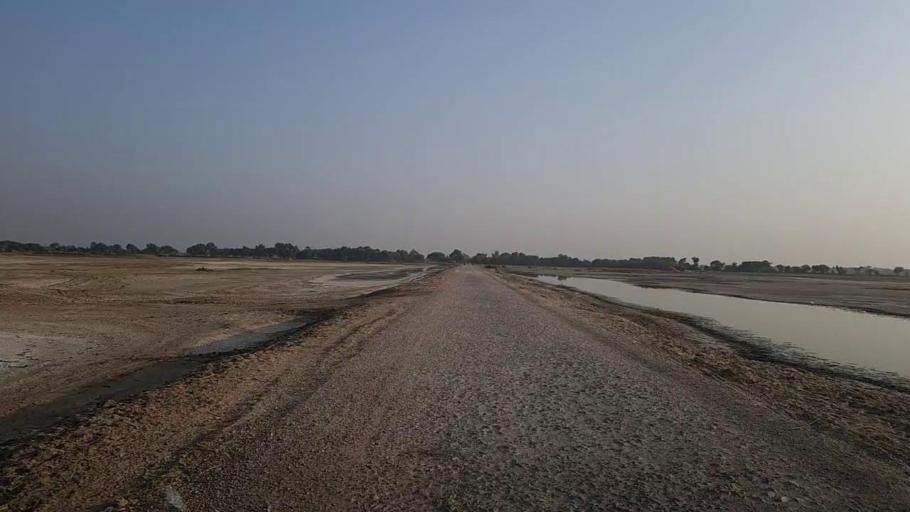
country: PK
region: Sindh
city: Kandhkot
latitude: 28.2465
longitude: 69.0905
